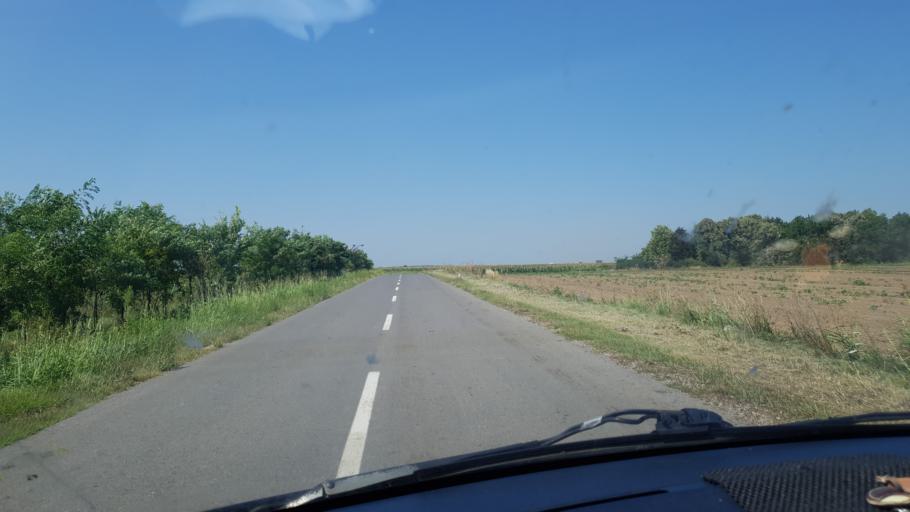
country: RS
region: Autonomna Pokrajina Vojvodina
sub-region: Juznobacki Okrug
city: Kovilj
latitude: 45.2151
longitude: 20.0621
